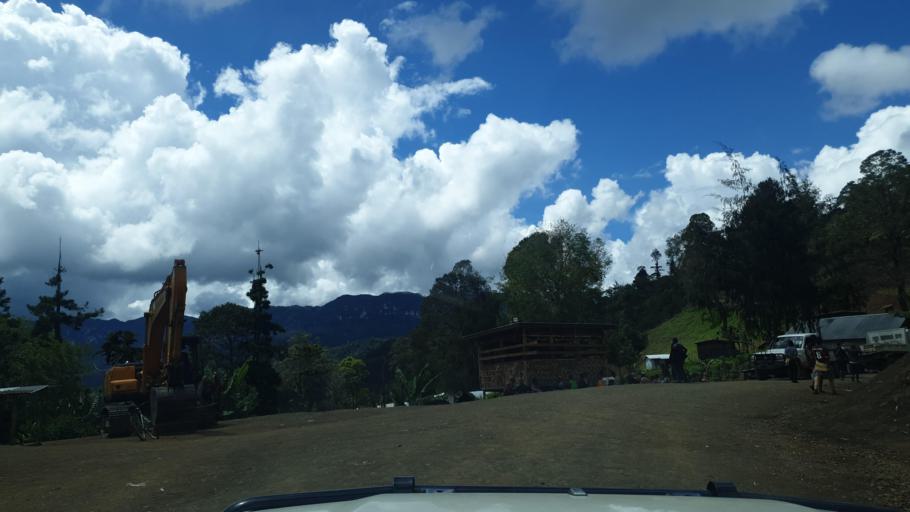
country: PG
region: Eastern Highlands
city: Goroka
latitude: -6.2783
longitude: 145.1848
